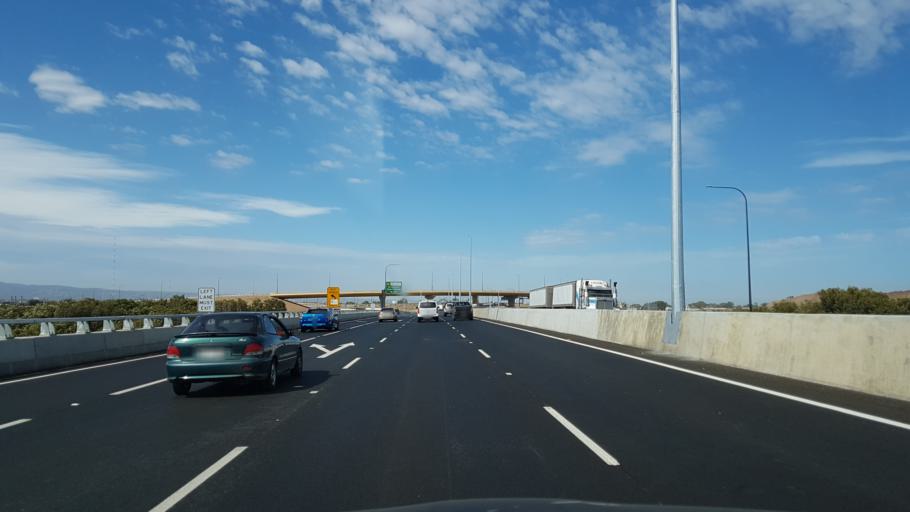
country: AU
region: South Australia
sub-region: Port Adelaide Enfield
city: Blair Athol
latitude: -34.8247
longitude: 138.5625
